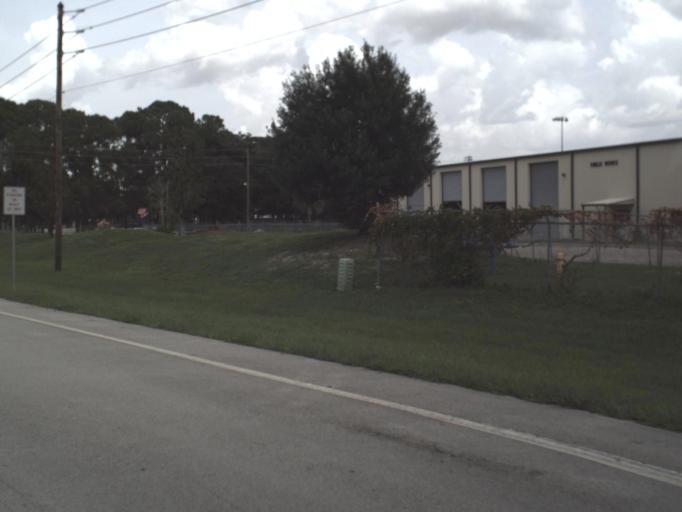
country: US
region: Florida
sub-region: Highlands County
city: Avon Park
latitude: 27.5659
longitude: -81.5135
